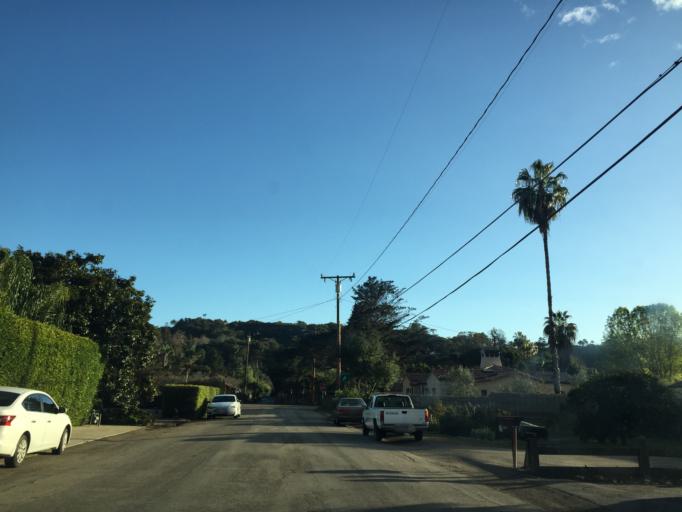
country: US
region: California
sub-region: Santa Barbara County
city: Goleta
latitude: 34.4372
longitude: -119.7731
